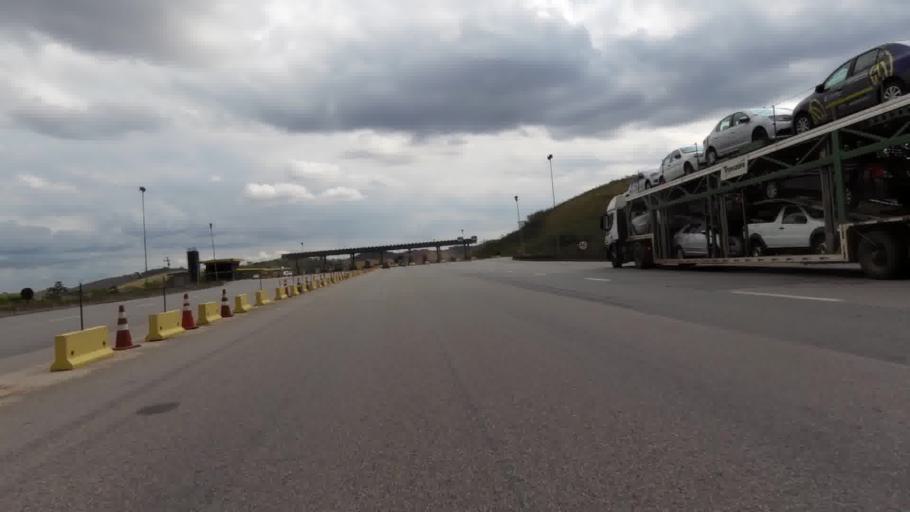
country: BR
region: Rio de Janeiro
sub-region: Casimiro De Abreu
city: Casimiro de Abreu
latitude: -22.4746
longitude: -42.0877
